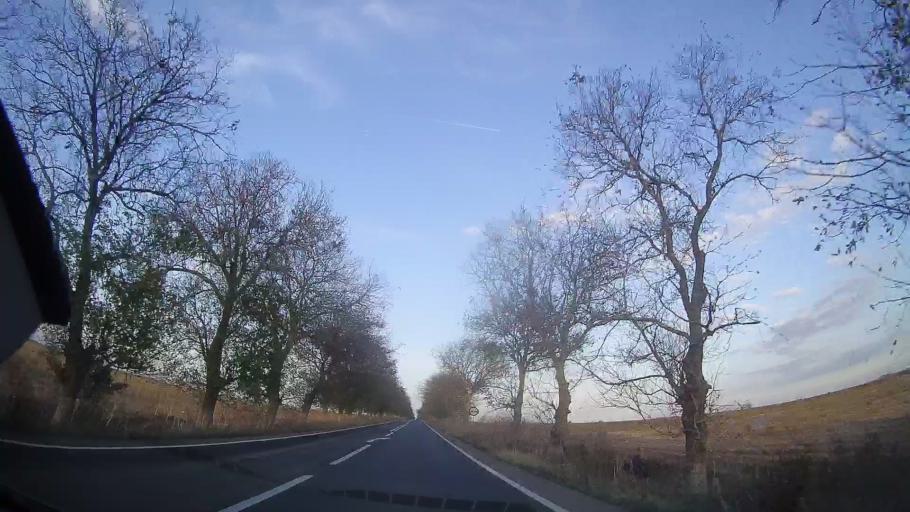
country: RO
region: Constanta
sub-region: Comuna Chirnogeni
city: Chirnogeni
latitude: 43.8530
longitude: 28.2457
